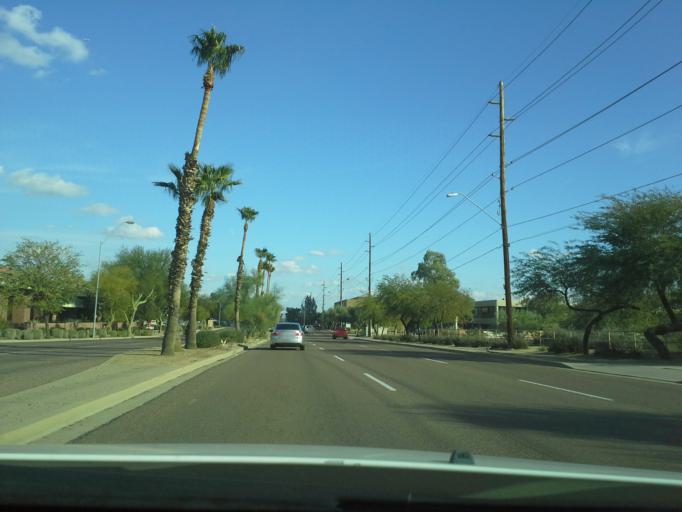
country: US
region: Arizona
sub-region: Maricopa County
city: Paradise Valley
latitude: 33.5826
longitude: -111.9845
